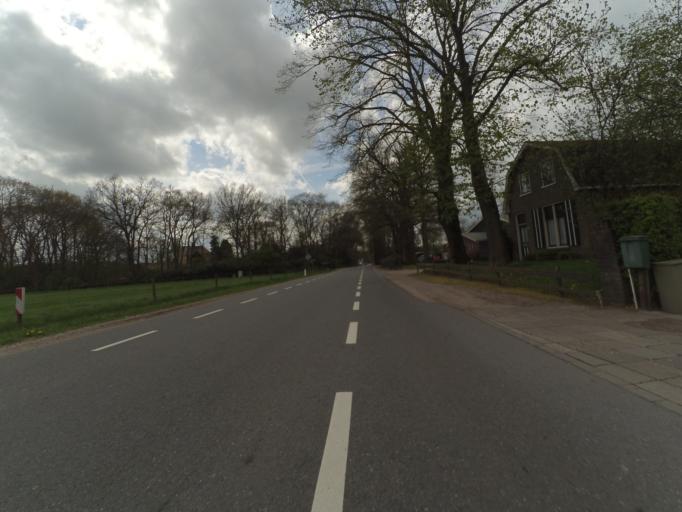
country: NL
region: Gelderland
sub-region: Gemeente Ede
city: Lunteren
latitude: 52.1072
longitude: 5.6410
